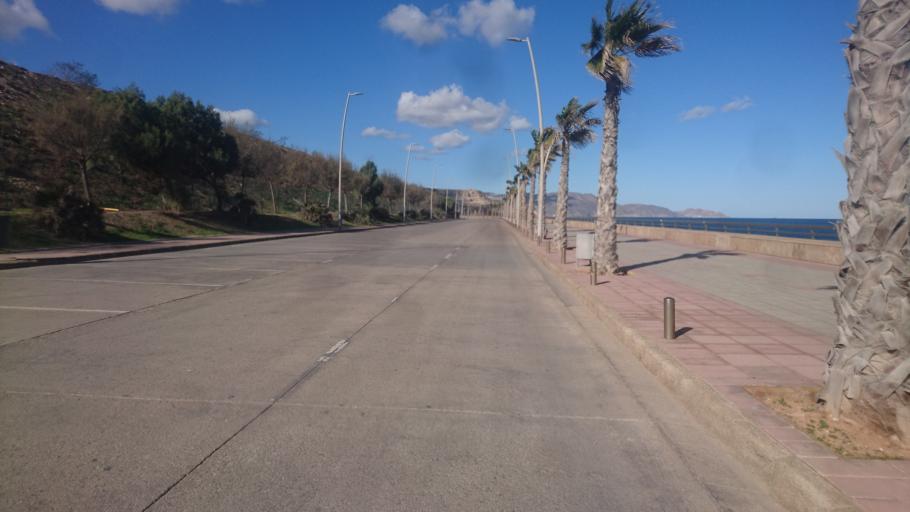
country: ES
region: Melilla
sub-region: Melilla
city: Melilla
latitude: 35.3003
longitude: -2.9366
